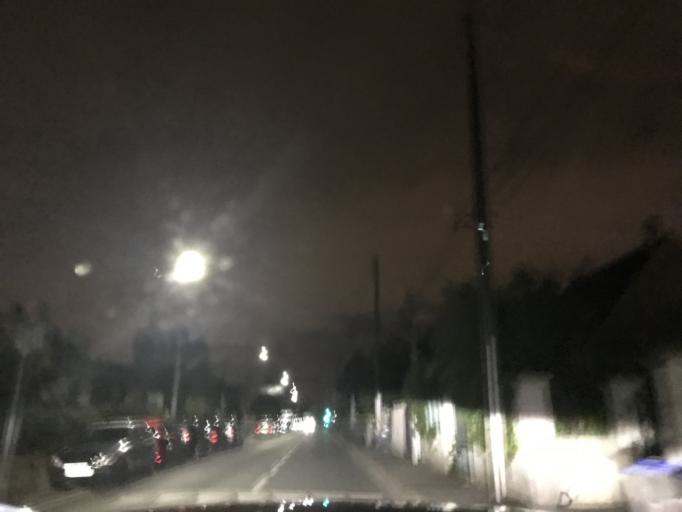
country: FR
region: Ile-de-France
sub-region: Departement des Yvelines
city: Sartrouville
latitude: 48.9383
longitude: 2.1946
